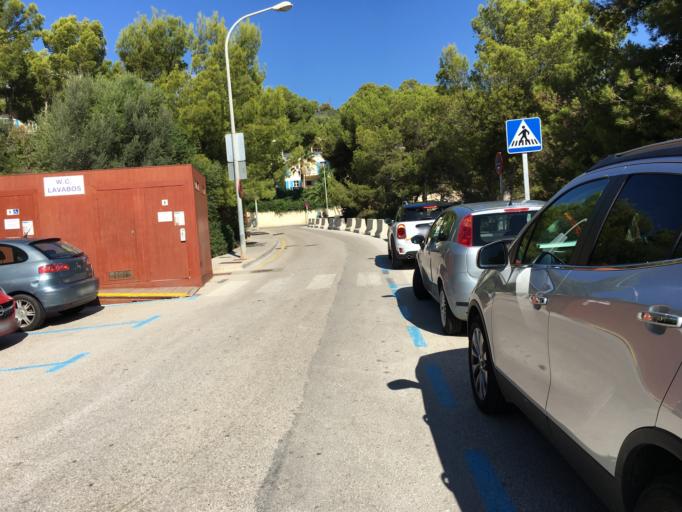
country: ES
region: Balearic Islands
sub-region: Illes Balears
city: Magaluf
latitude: 39.5343
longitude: 2.5891
